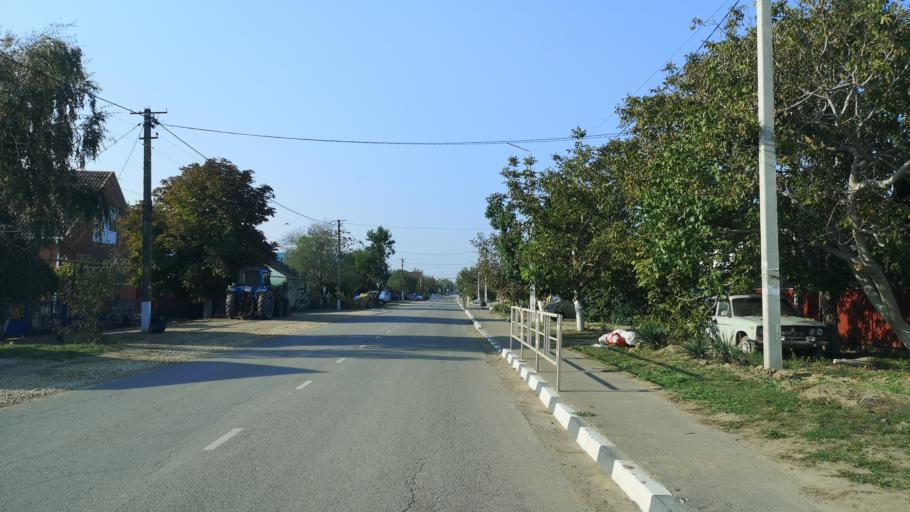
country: RU
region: Krasnodarskiy
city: Taman'
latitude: 45.2131
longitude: 36.7020
